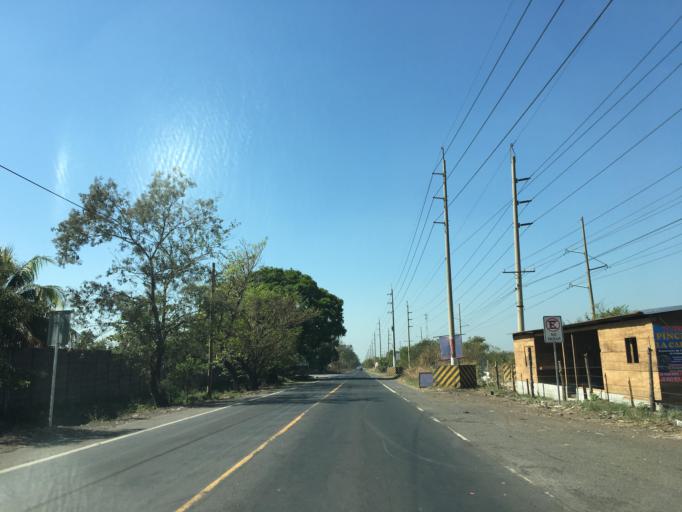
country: GT
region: Escuintla
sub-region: Municipio de Masagua
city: Masagua
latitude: 14.2345
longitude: -90.8214
